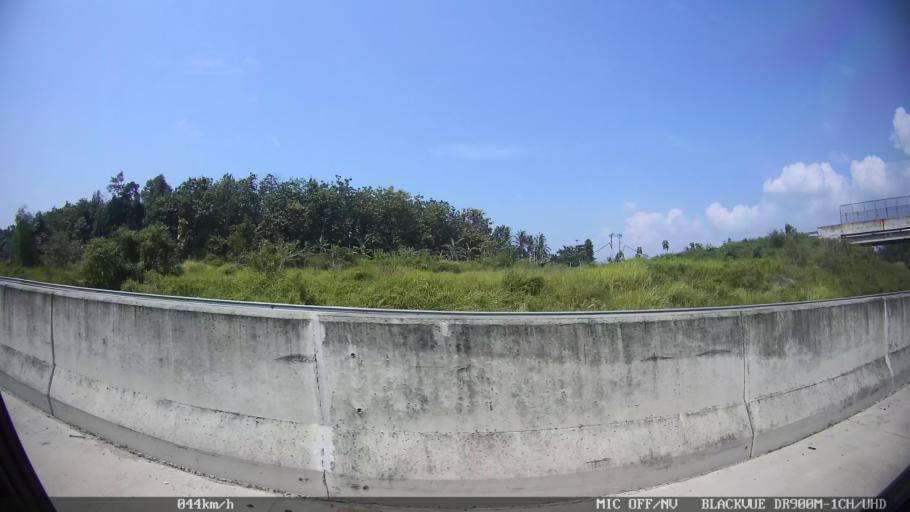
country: ID
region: Lampung
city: Kedaton
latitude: -5.3210
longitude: 105.2709
